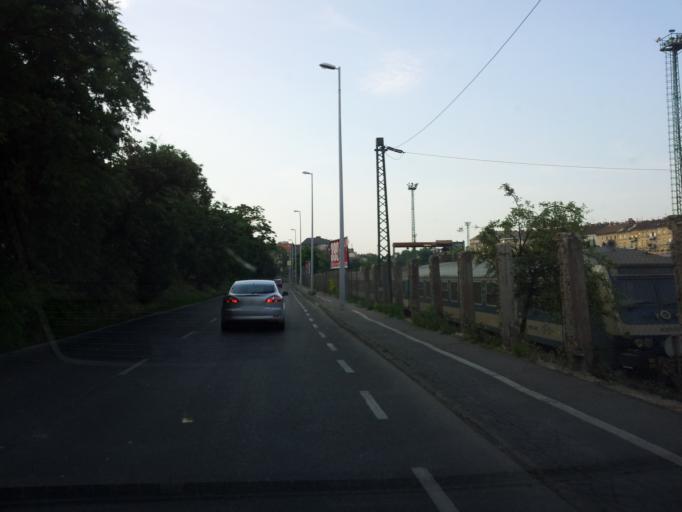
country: HU
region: Budapest
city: Budapest I. keruelet
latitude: 47.4939
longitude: 19.0291
